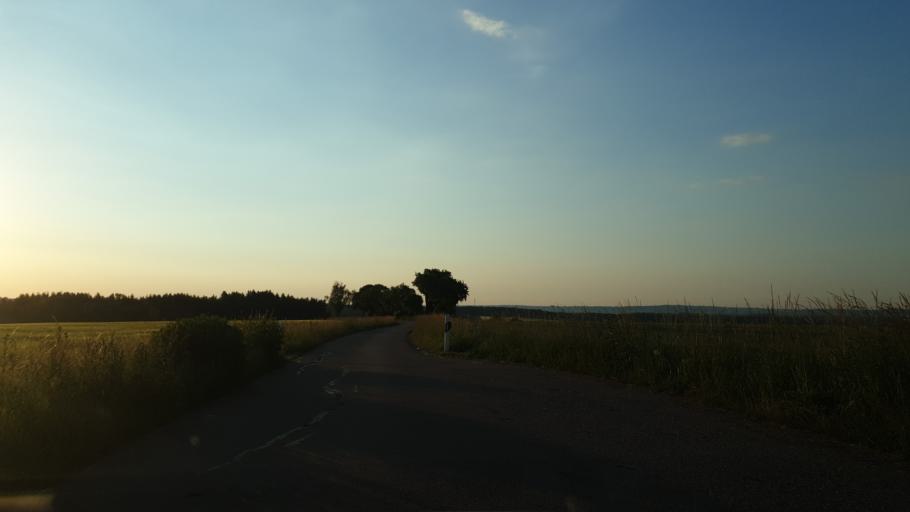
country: DE
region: Saxony
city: Oelsnitz
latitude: 50.6850
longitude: 12.7318
